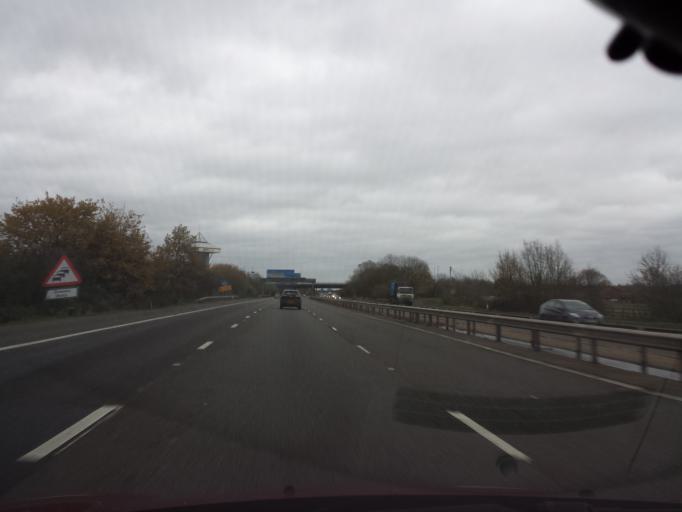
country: GB
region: England
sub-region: Surrey
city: Sunbury-on-Thames
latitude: 51.4115
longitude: -0.4356
